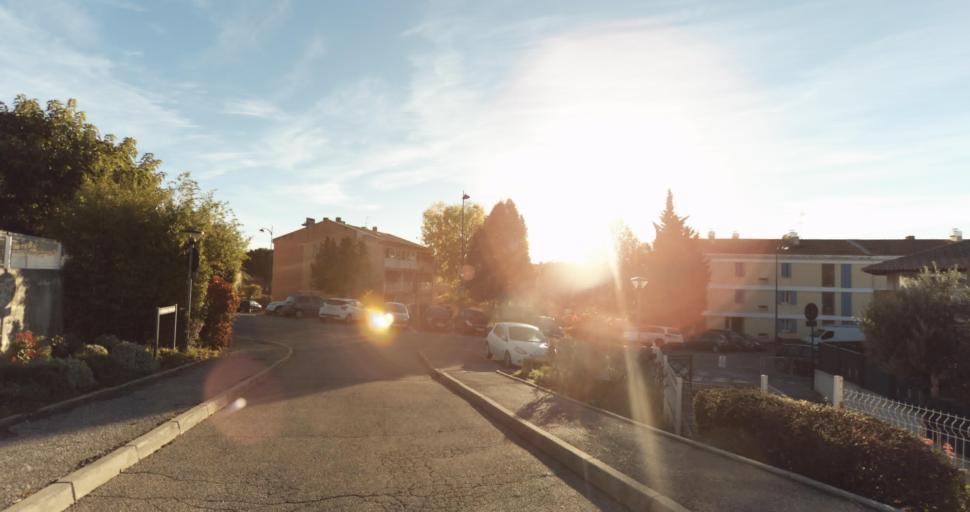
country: FR
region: Provence-Alpes-Cote d'Azur
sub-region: Departement des Bouches-du-Rhone
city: Venelles
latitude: 43.5978
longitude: 5.4833
